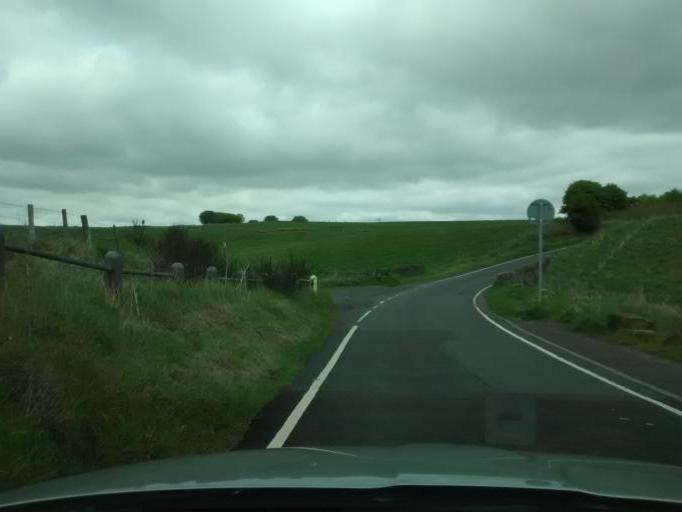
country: GB
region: Scotland
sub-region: West Lothian
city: Armadale
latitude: 55.8862
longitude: -3.7176
